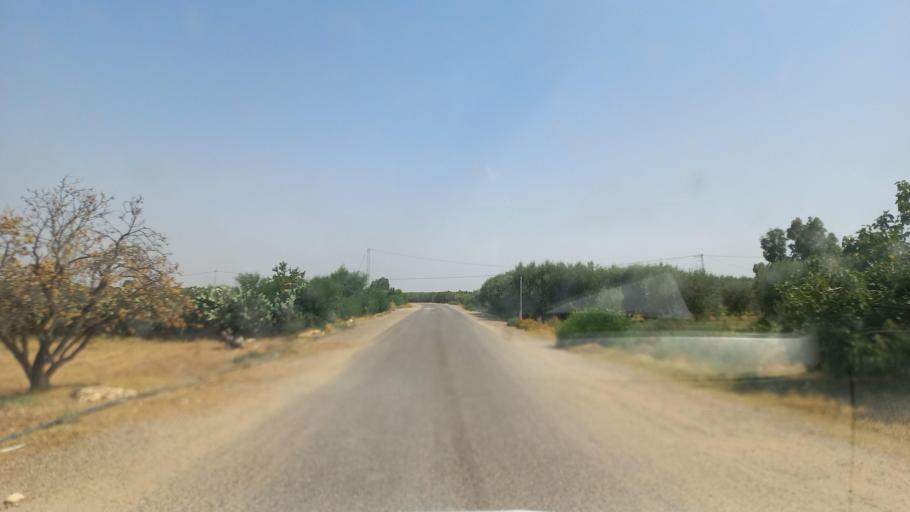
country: TN
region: Al Qasrayn
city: Kasserine
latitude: 35.2373
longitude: 9.0346
